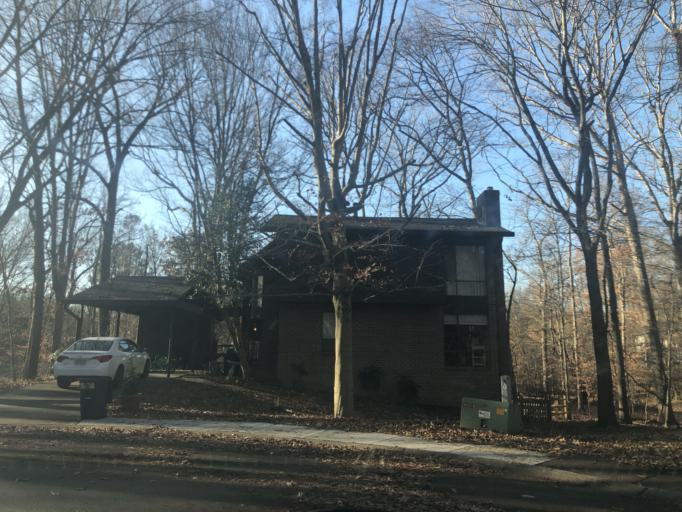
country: US
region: Maryland
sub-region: Howard County
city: Columbia
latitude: 39.2048
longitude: -76.8403
